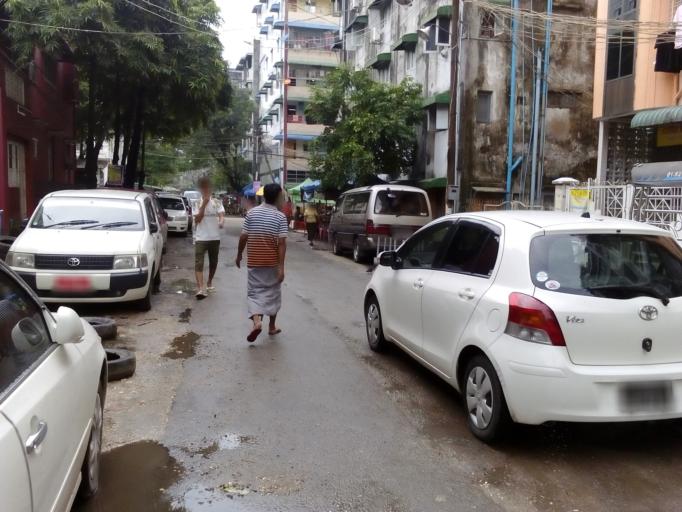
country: MM
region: Yangon
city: Yangon
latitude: 16.7989
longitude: 96.1767
